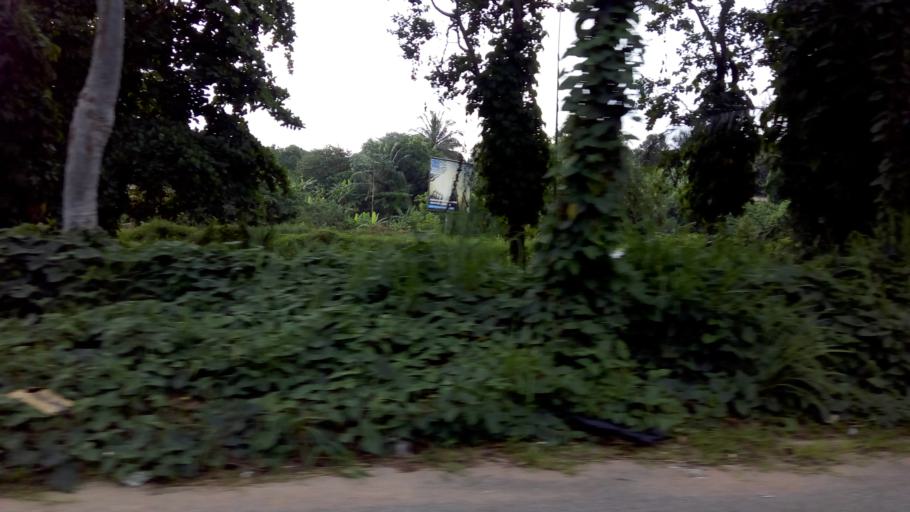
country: CI
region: Lagunes
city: Abidjan
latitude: 5.3478
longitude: -4.0049
